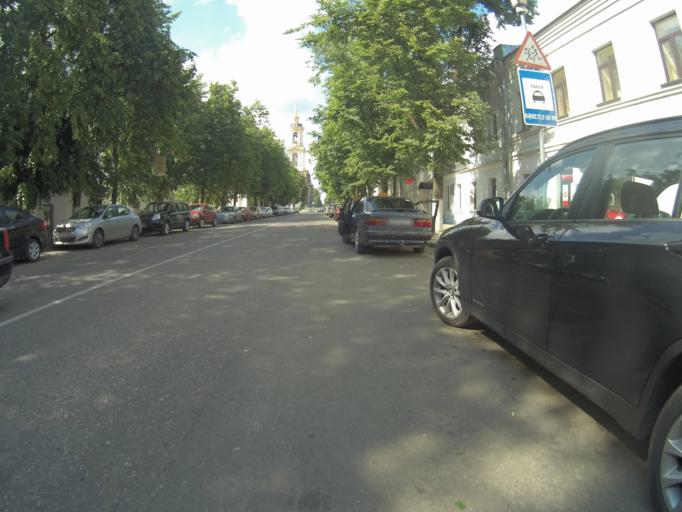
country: RU
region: Vladimir
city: Suzdal'
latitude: 56.4223
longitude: 40.4483
